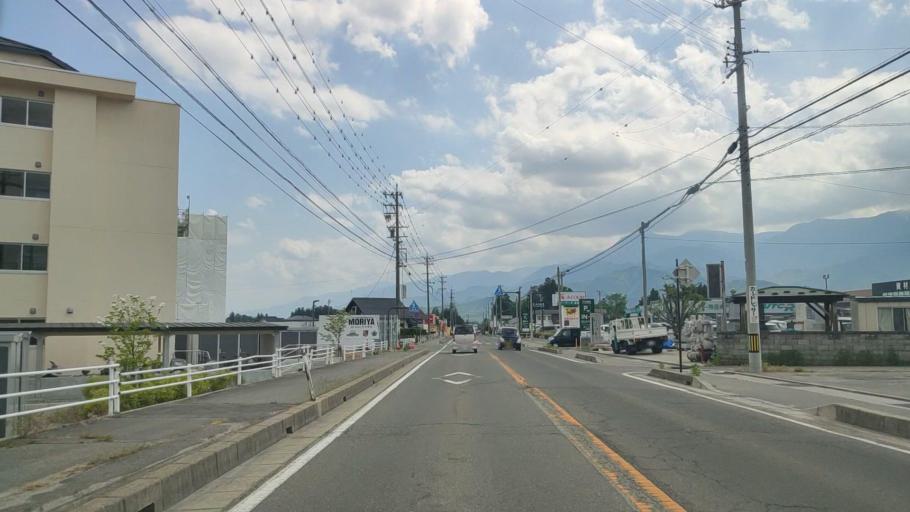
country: JP
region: Nagano
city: Omachi
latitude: 36.4786
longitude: 137.8499
